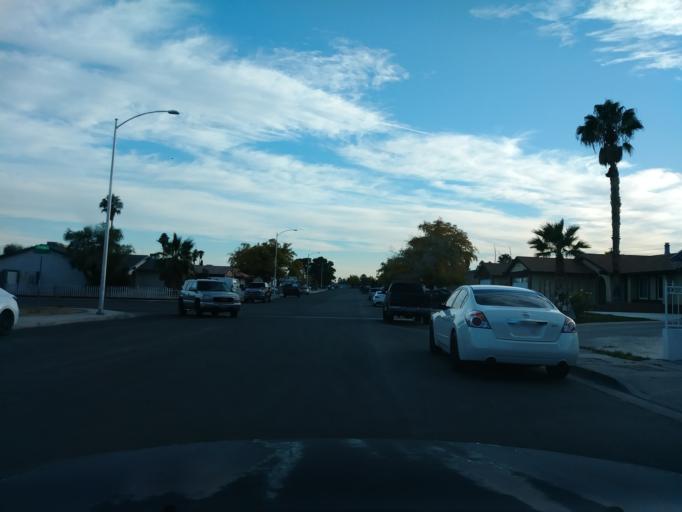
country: US
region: Nevada
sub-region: Clark County
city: Spring Valley
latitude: 36.1698
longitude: -115.2413
